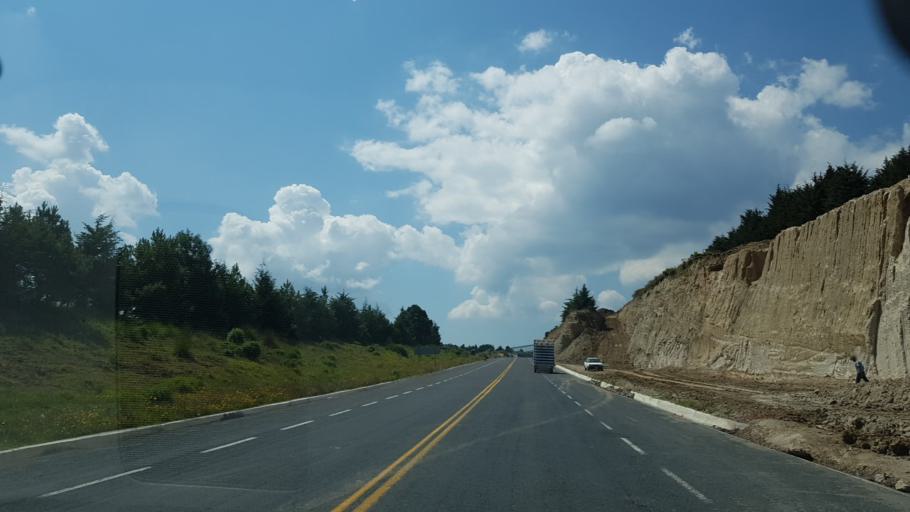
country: MX
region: Mexico
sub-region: Villa Victoria
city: Colonia Doctor Gustavo Baz
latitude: 19.3684
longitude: -99.9396
